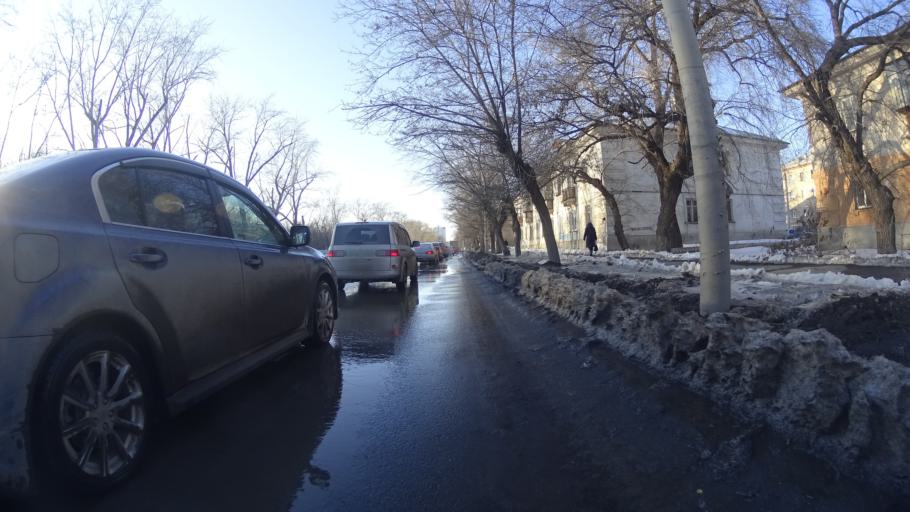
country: RU
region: Chelyabinsk
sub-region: Gorod Chelyabinsk
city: Chelyabinsk
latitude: 55.1333
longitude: 61.4605
